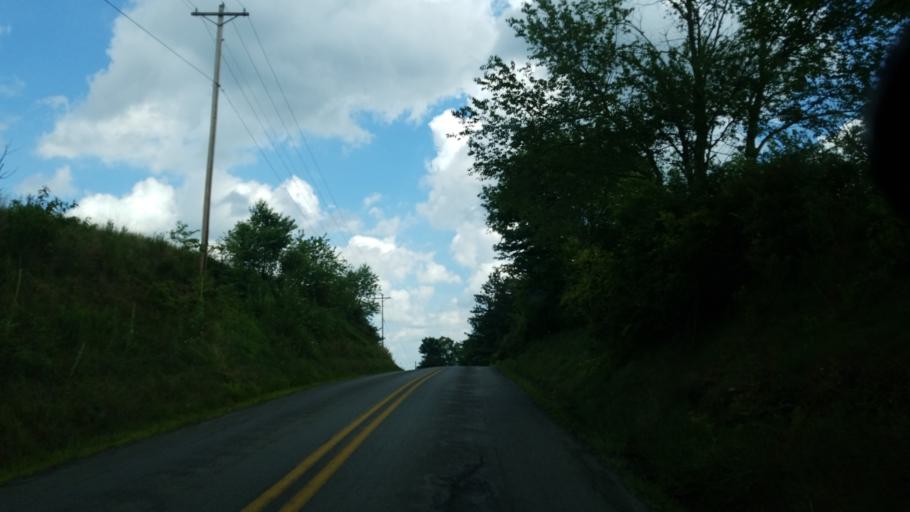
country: US
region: Pennsylvania
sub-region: Jefferson County
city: Brookville
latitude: 41.2283
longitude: -79.0963
